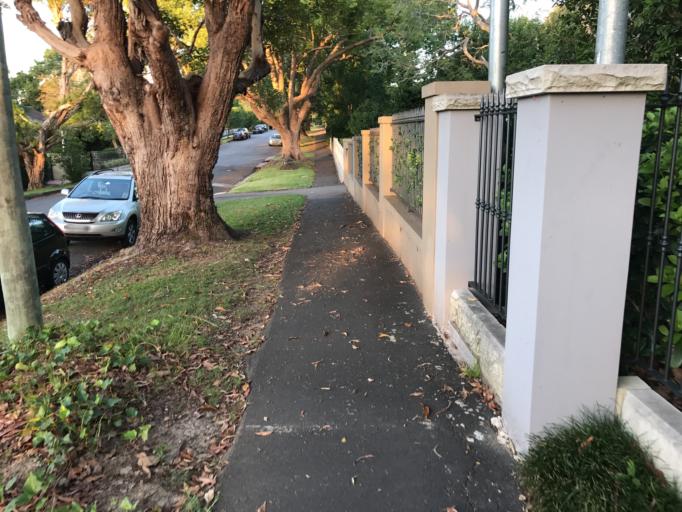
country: AU
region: New South Wales
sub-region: Ku-ring-gai
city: Killara
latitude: -33.7629
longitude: 151.1668
